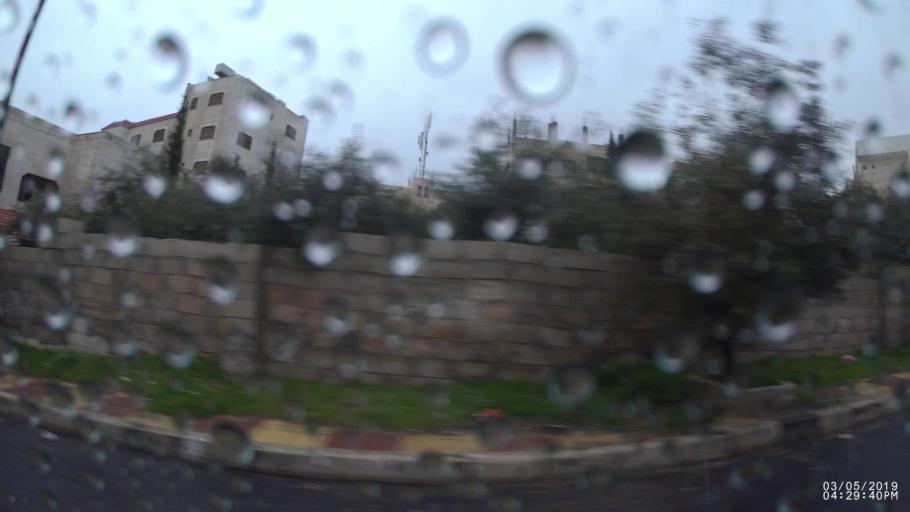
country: JO
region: Amman
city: Amman
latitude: 32.0009
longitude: 35.9647
